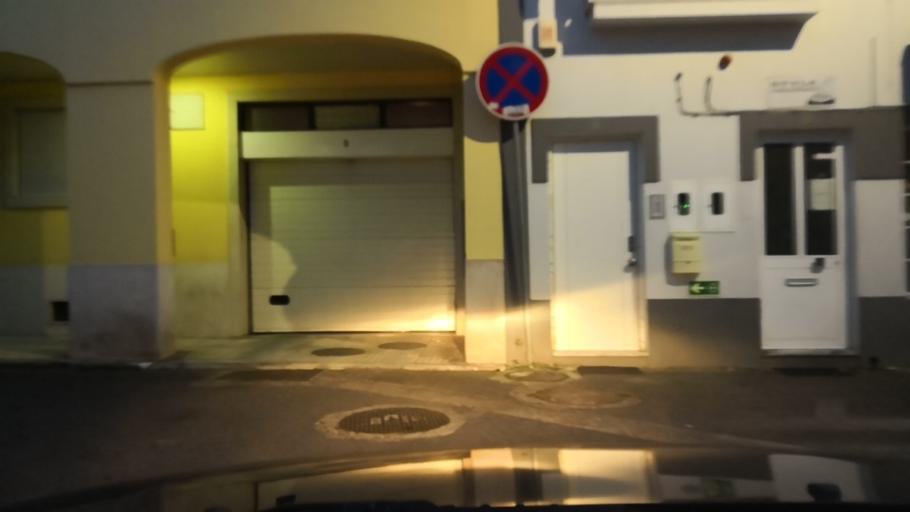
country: PT
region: Setubal
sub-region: Setubal
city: Setubal
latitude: 38.5264
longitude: -8.8877
